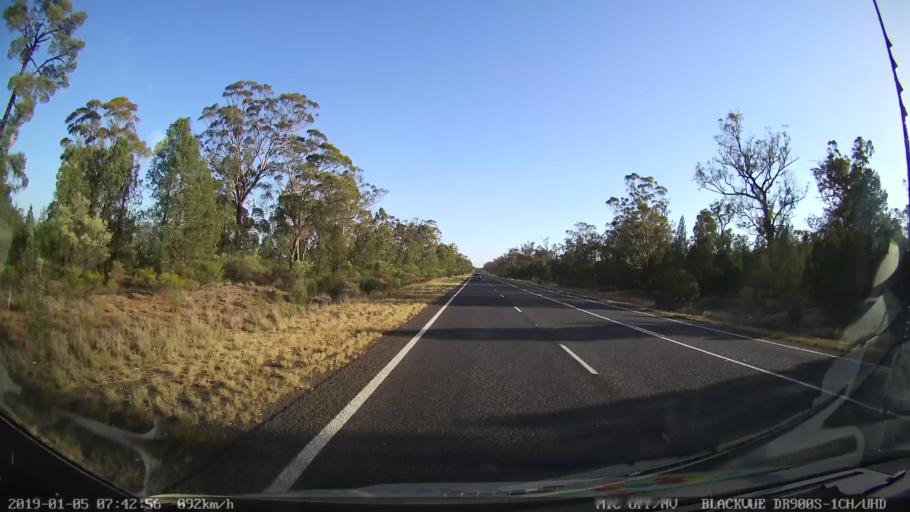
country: AU
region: New South Wales
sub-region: Gilgandra
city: Gilgandra
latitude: -31.8915
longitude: 148.6304
